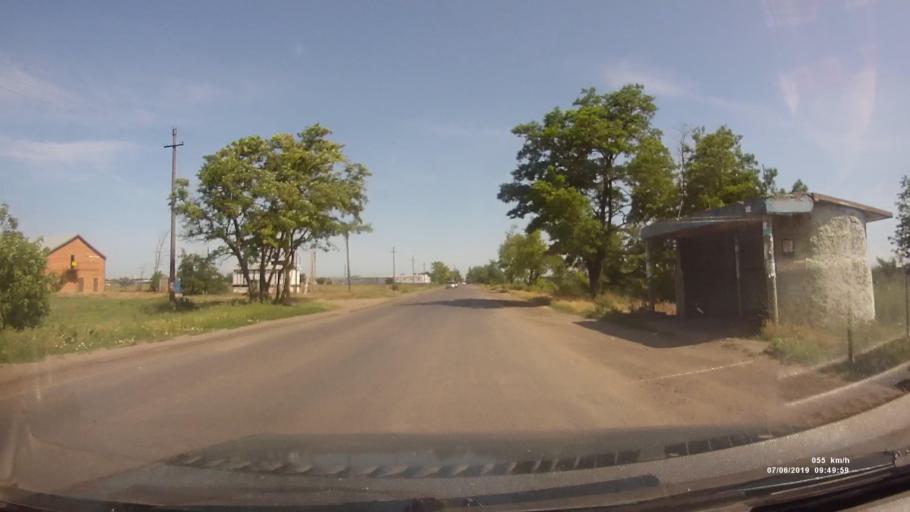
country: RU
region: Rostov
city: Azov
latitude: 47.0753
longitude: 39.4377
